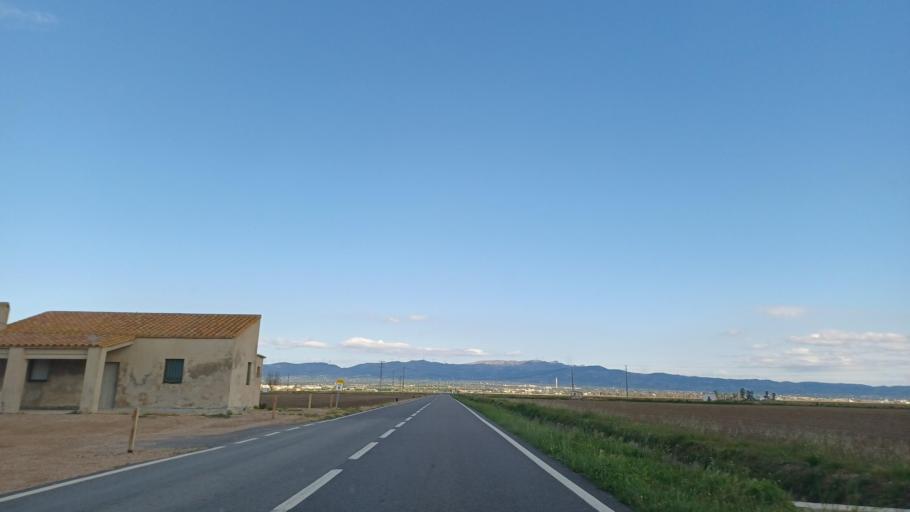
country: ES
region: Catalonia
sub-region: Provincia de Tarragona
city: Deltebre
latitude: 40.7569
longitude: 0.7013
